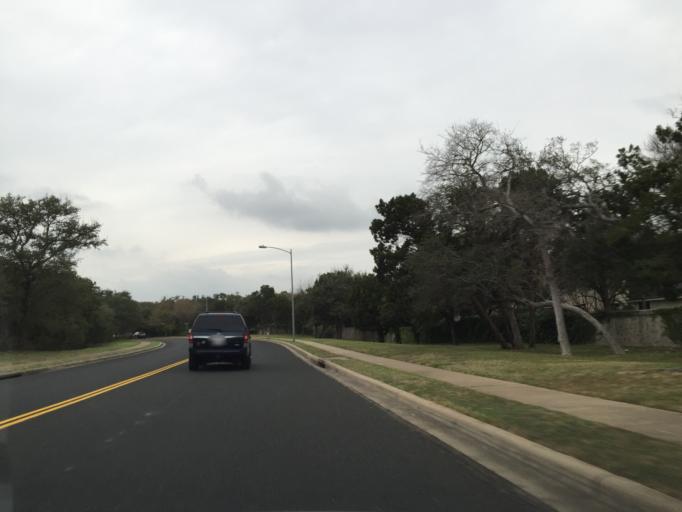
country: US
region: Texas
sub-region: Travis County
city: Rollingwood
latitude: 30.2427
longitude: -97.8315
